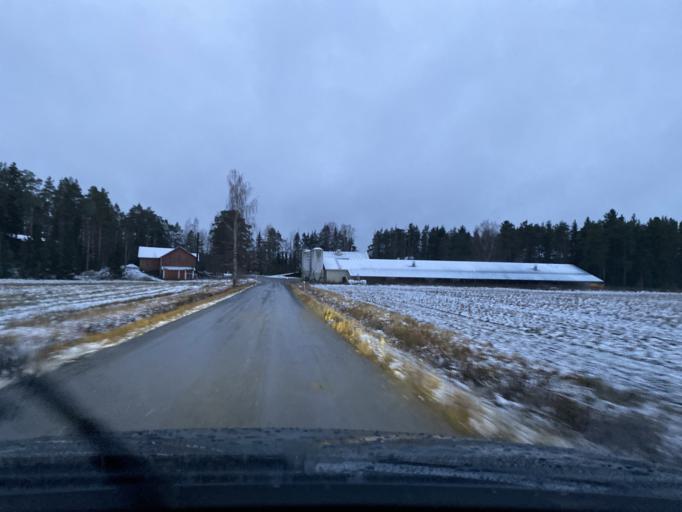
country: FI
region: Pirkanmaa
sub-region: Lounais-Pirkanmaa
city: Punkalaidun
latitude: 61.1444
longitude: 22.9659
